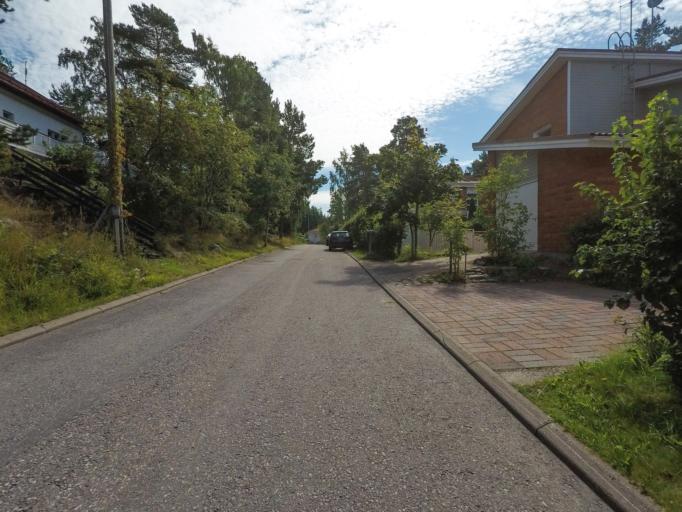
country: FI
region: Uusimaa
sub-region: Helsinki
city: Helsinki
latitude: 60.1620
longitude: 25.0610
